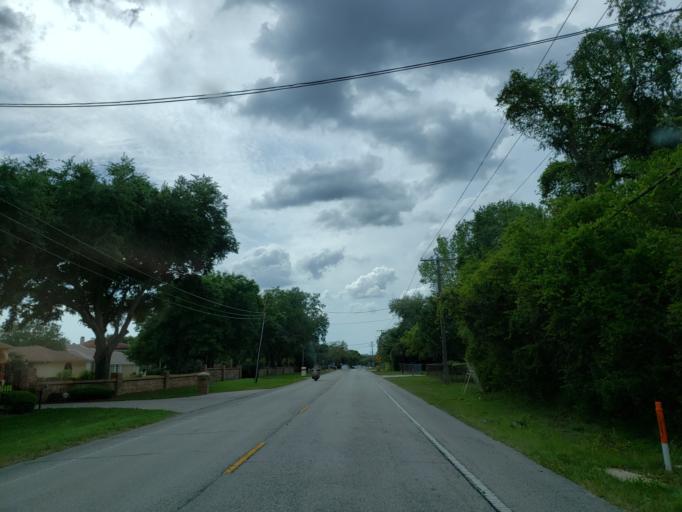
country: US
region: Florida
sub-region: Hillsborough County
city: Keystone
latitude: 28.1400
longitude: -82.6343
